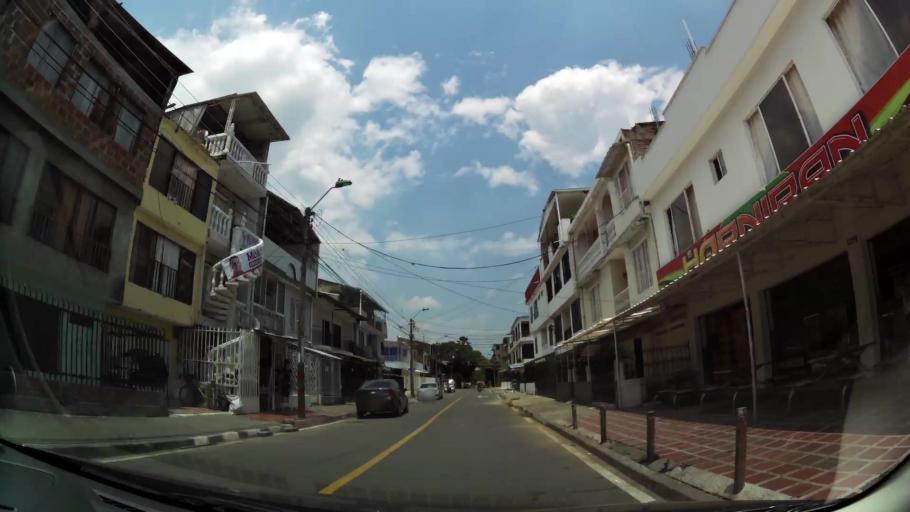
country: CO
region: Valle del Cauca
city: Cali
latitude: 3.4121
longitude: -76.5314
